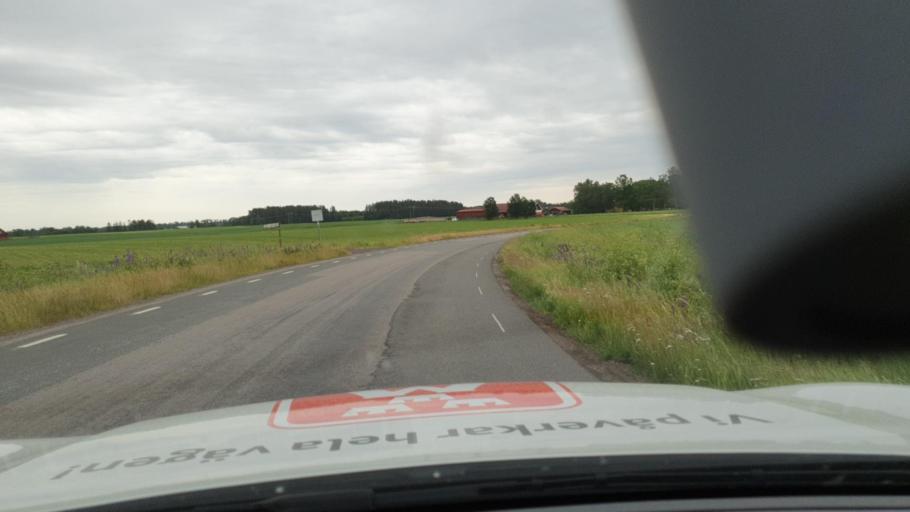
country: SE
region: Vaestra Goetaland
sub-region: Skovde Kommun
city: Skoevde
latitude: 58.3838
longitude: 13.9183
